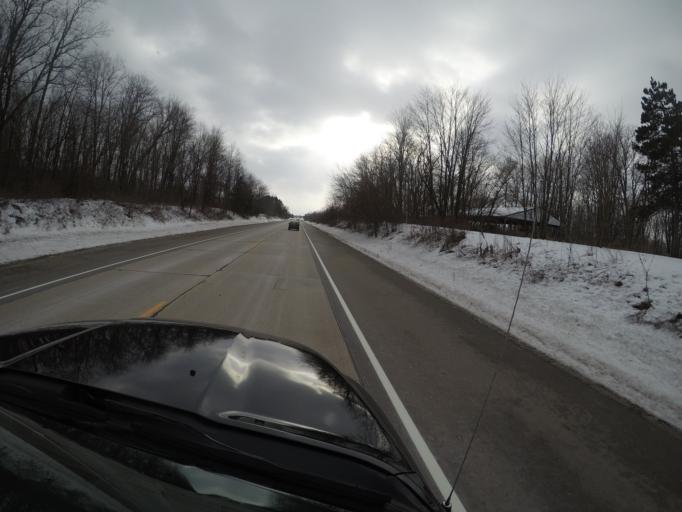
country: US
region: Wisconsin
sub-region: Trempealeau County
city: Galesville
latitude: 44.0396
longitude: -91.2907
